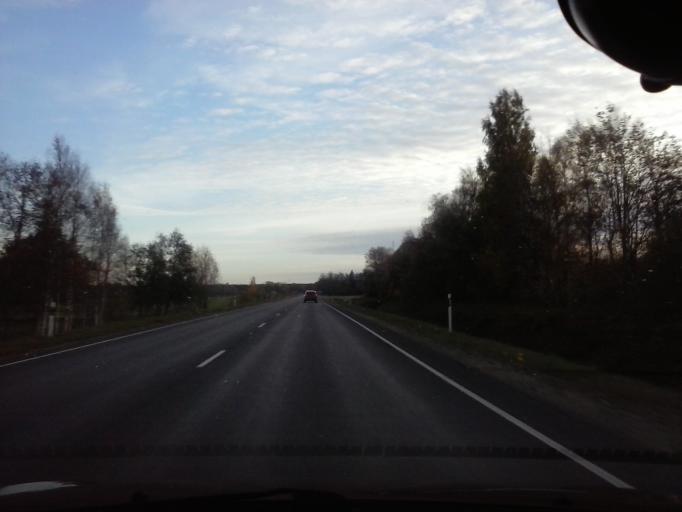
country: EE
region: Harju
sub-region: Nissi vald
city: Turba
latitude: 58.9108
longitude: 24.1112
